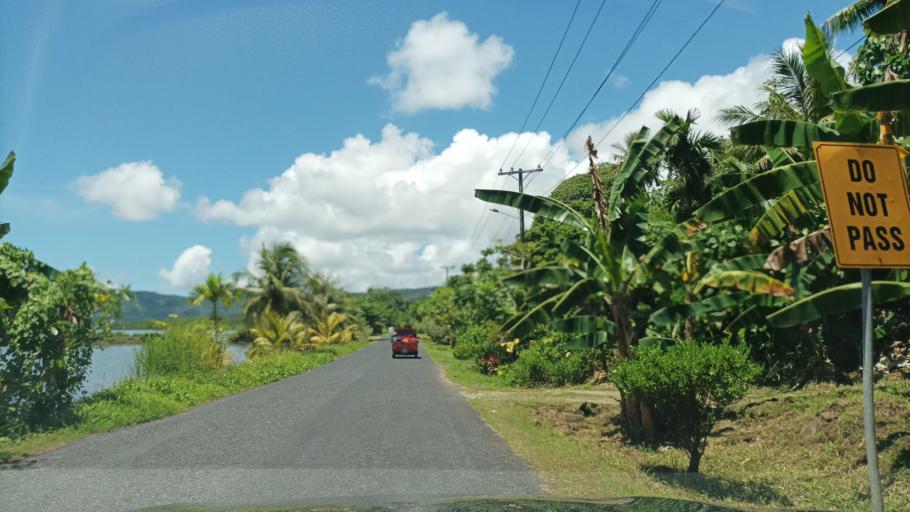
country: FM
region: Pohnpei
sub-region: Kolonia Municipality
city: Kolonia
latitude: 6.9554
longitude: 158.2778
